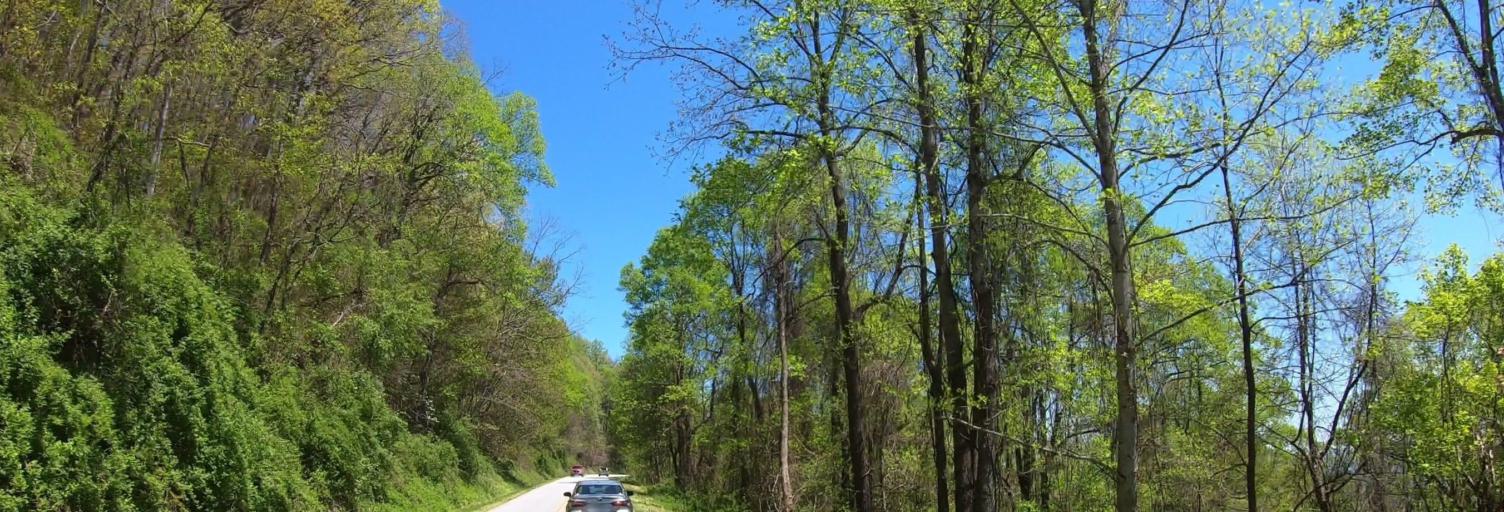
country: US
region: North Carolina
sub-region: Buncombe County
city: Avery Creek
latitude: 35.4721
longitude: -82.6161
